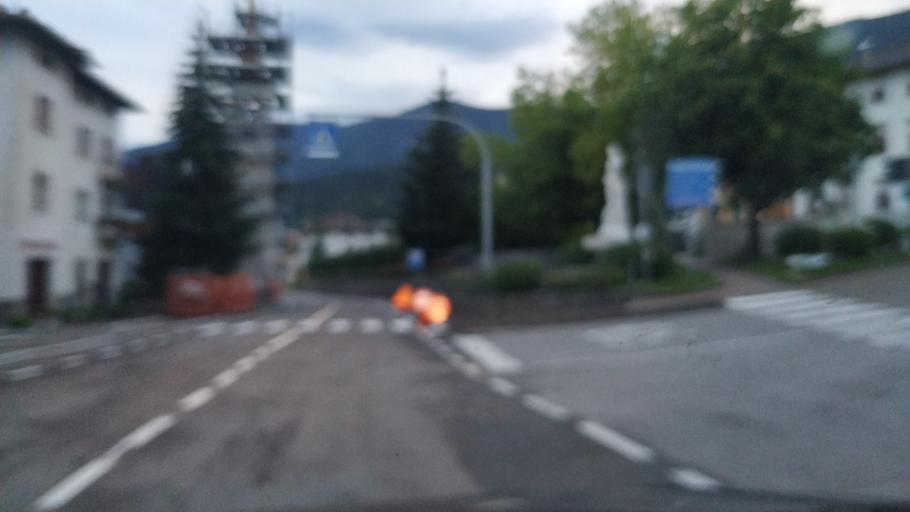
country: IT
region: Trentino-Alto Adige
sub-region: Provincia di Trento
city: Brez
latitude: 46.4310
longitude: 11.1074
